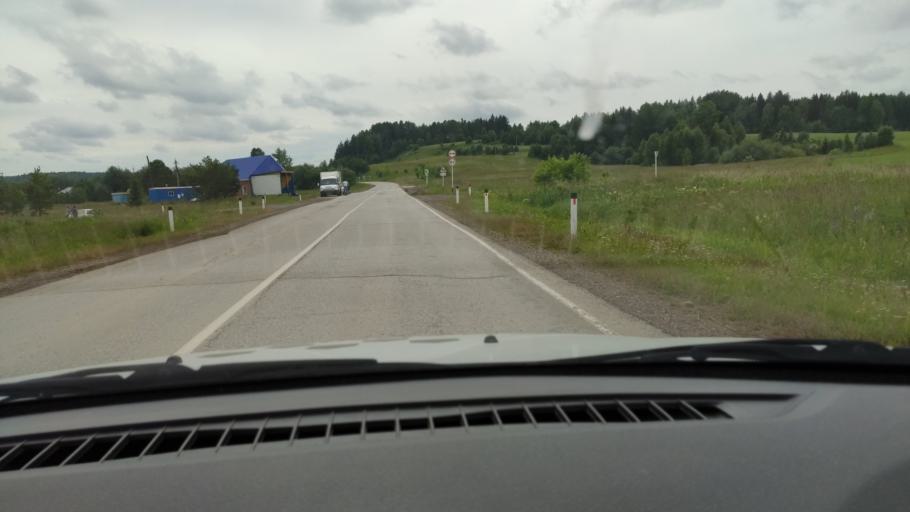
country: RU
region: Perm
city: Kukushtan
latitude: 57.4988
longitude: 56.6458
